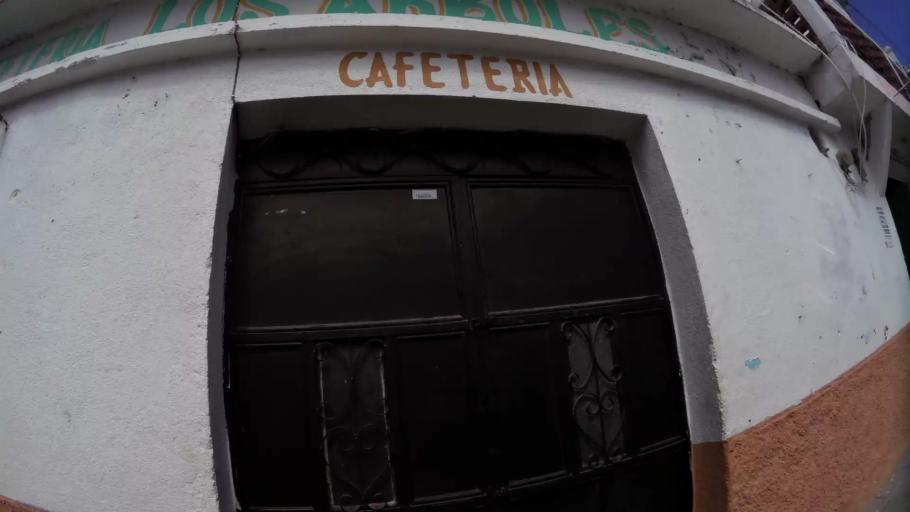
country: GT
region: Solola
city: Panajachel
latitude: 14.7459
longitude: -91.1543
